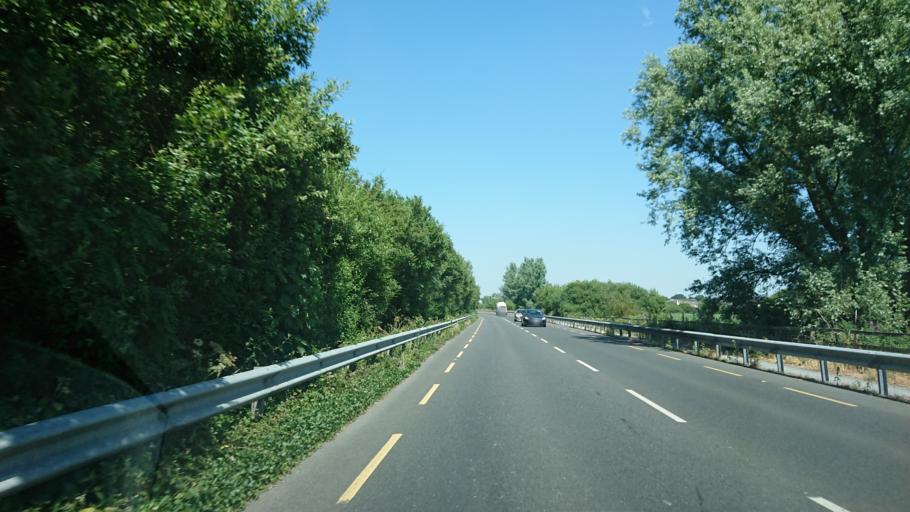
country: IE
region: Munster
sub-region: Waterford
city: Waterford
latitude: 52.2292
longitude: -7.1230
